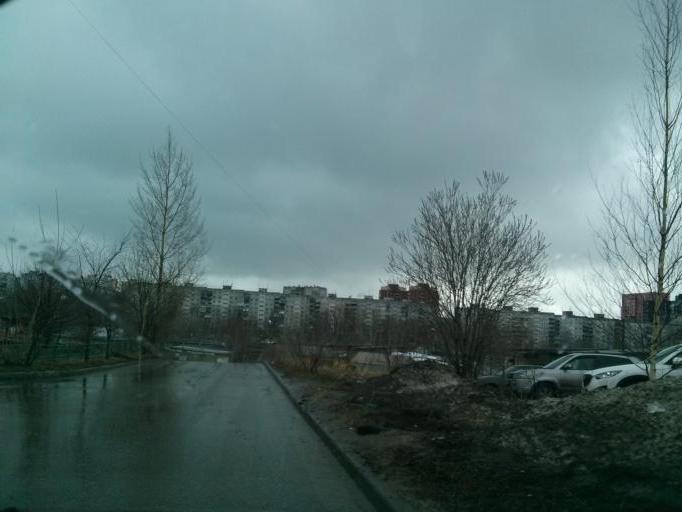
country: RU
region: Nizjnij Novgorod
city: Afonino
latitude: 56.3027
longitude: 44.0662
